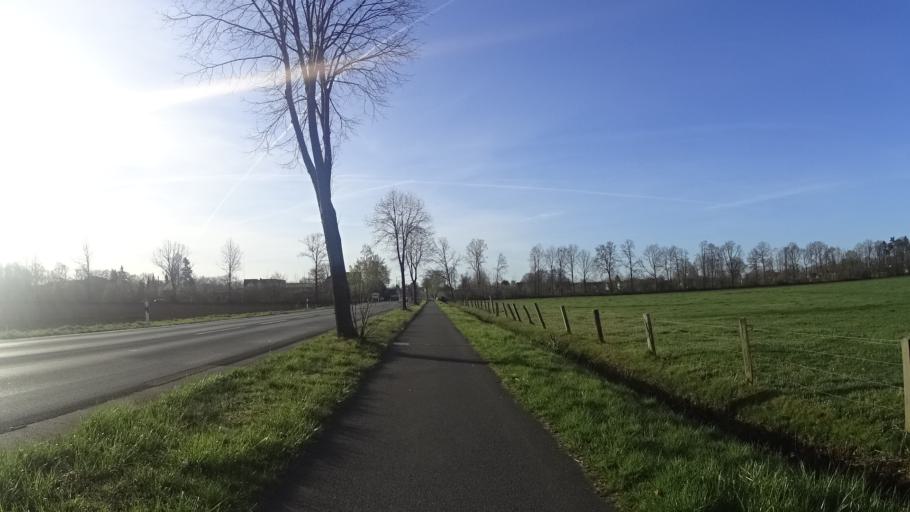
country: DE
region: North Rhine-Westphalia
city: Emsdetten
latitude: 52.1385
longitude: 7.5409
